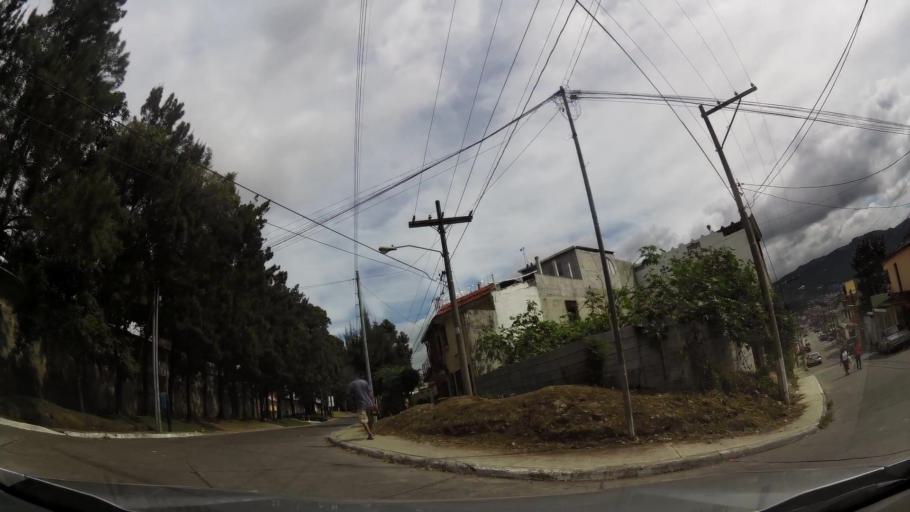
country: GT
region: Guatemala
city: Santa Catarina Pinula
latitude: 14.5663
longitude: -90.5376
